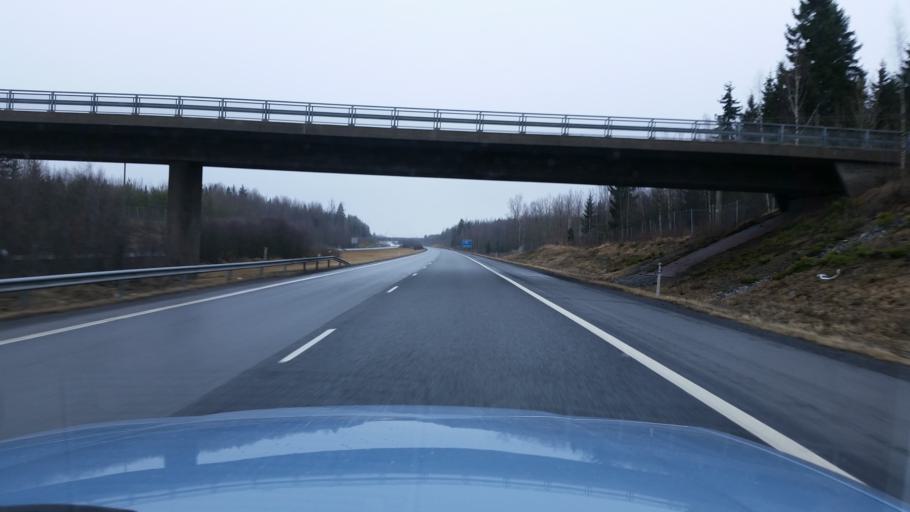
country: FI
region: Pirkanmaa
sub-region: Etelae-Pirkanmaa
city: Toijala
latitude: 61.2365
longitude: 23.8367
